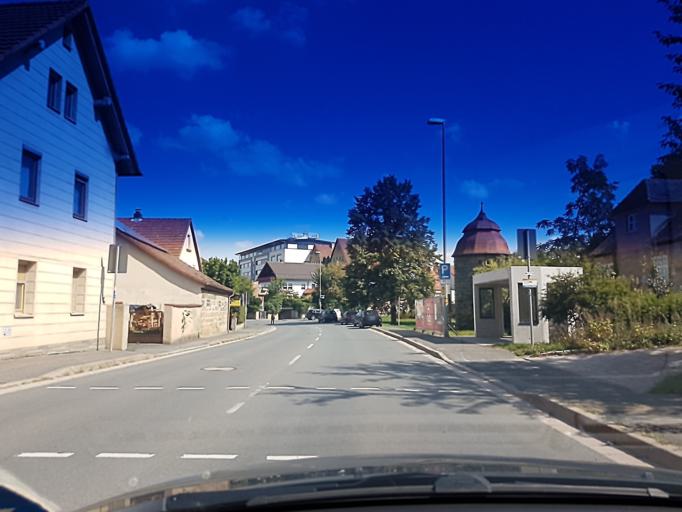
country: DE
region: Bavaria
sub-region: Upper Franconia
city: Weismain
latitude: 50.0859
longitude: 11.2394
